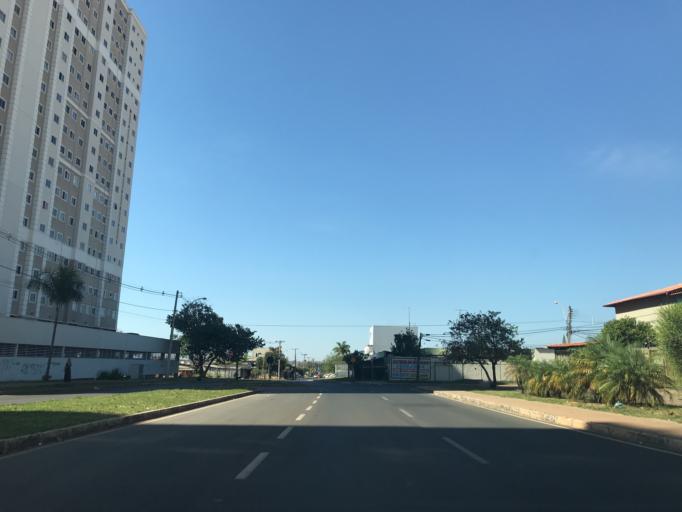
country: BR
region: Federal District
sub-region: Brasilia
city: Brasilia
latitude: -15.8127
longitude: -48.0819
